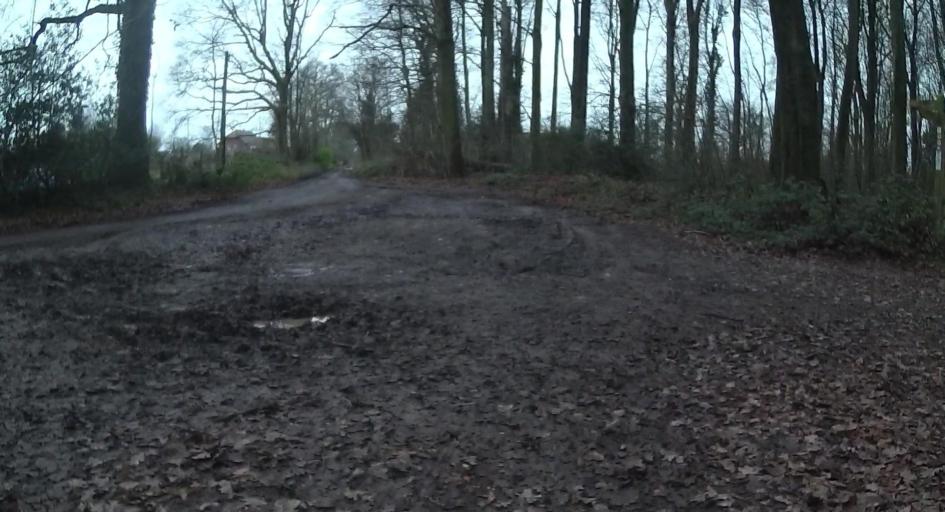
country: GB
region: England
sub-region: Hampshire
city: Four Marks
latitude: 51.1114
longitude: -1.0297
